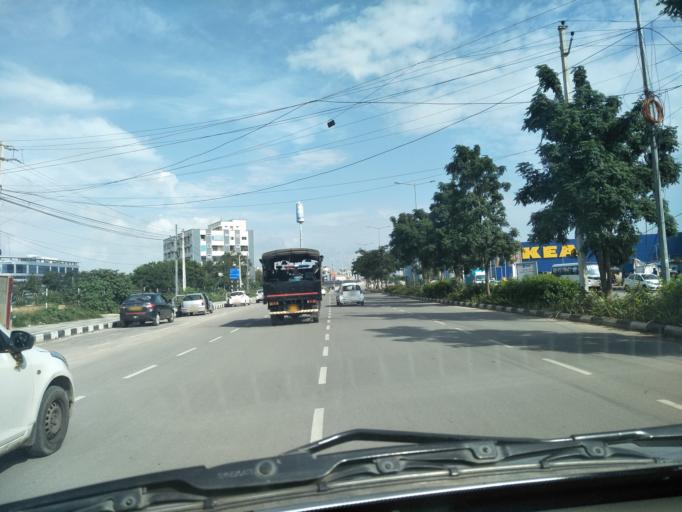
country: IN
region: Telangana
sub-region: Rangareddi
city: Kukatpalli
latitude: 17.4410
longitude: 78.3748
